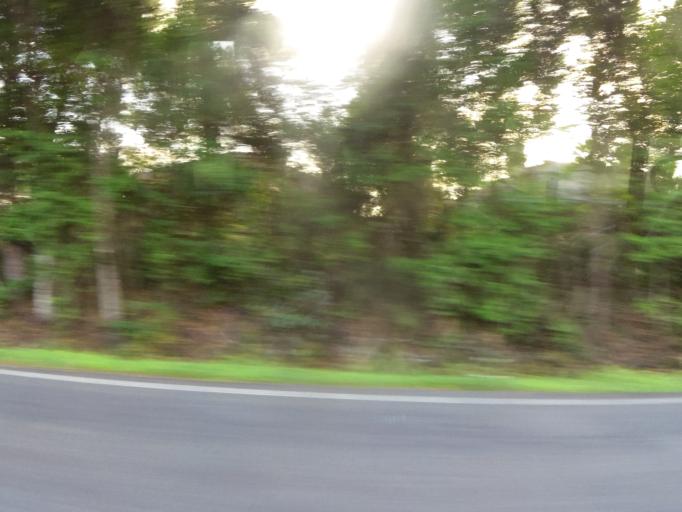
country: US
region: Florida
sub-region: Saint Johns County
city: Fruit Cove
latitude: 30.1289
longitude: -81.6170
